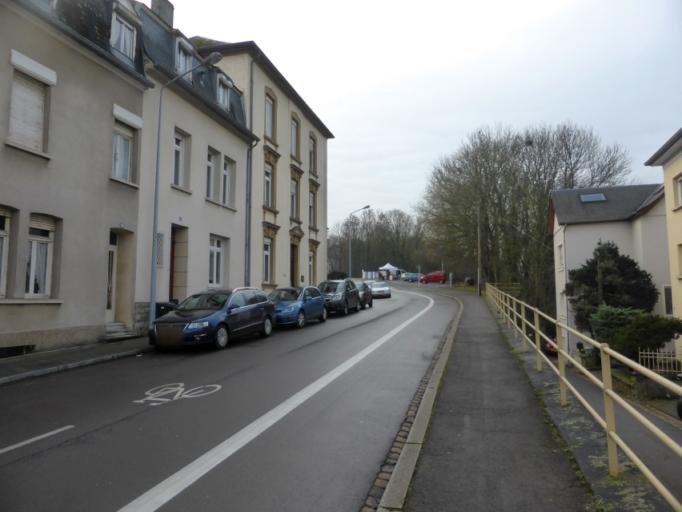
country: LU
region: Luxembourg
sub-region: Canton de Luxembourg
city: Luxembourg
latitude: 49.6085
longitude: 6.1430
